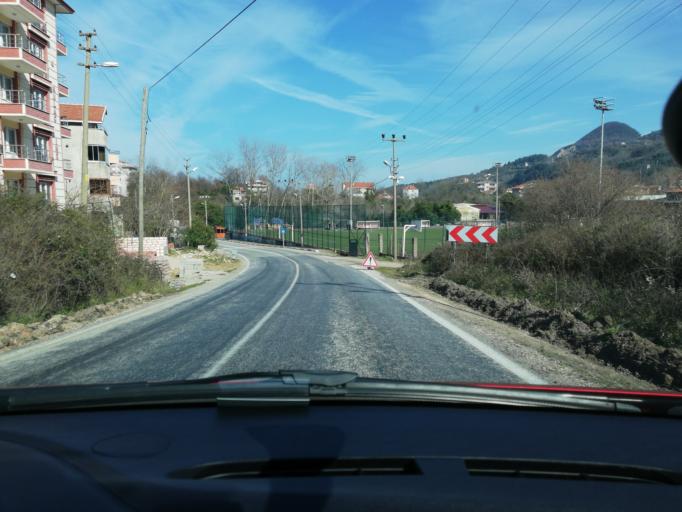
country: TR
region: Bartin
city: Kurucasile
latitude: 41.8423
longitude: 32.7143
